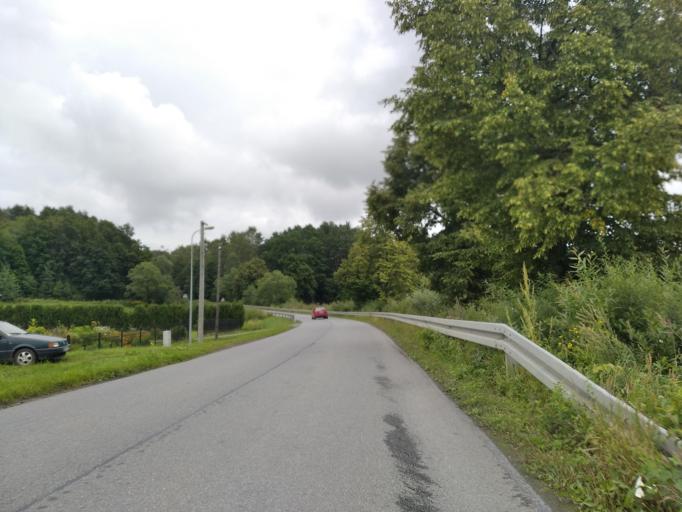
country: PL
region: Subcarpathian Voivodeship
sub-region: Powiat przemyski
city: Bircza
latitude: 49.6795
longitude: 22.4106
